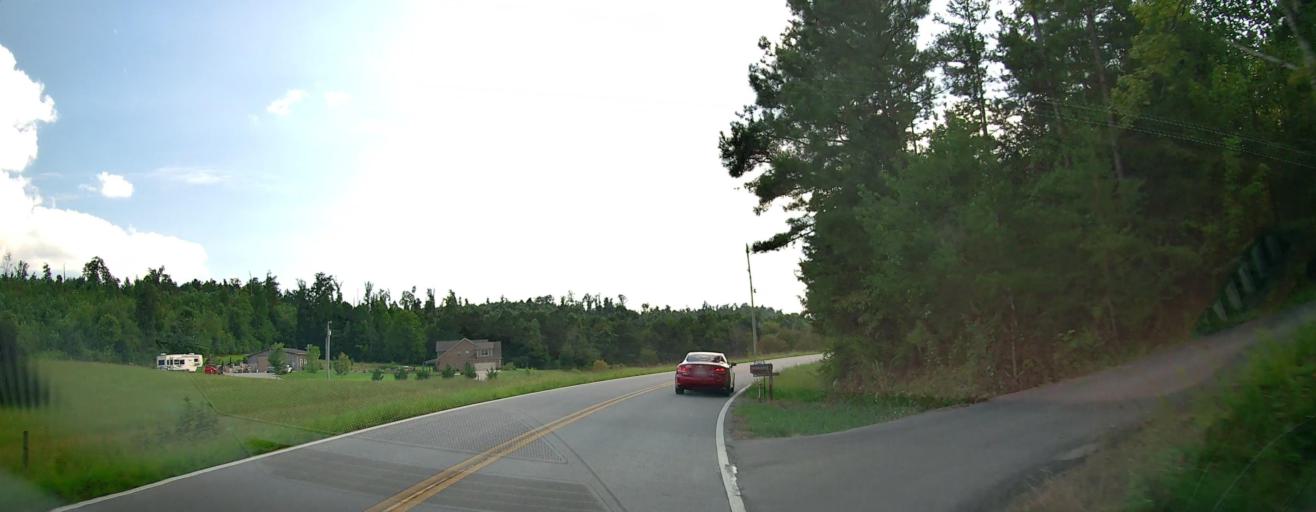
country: US
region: Georgia
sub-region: Catoosa County
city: Ringgold
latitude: 34.9609
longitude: -85.0703
